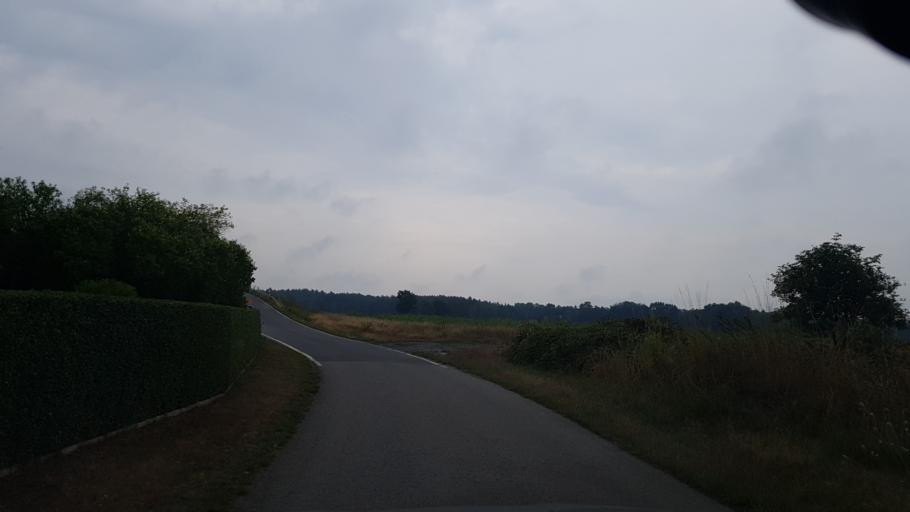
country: DE
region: Saxony
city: Bernsdorf
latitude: 51.3716
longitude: 14.0789
